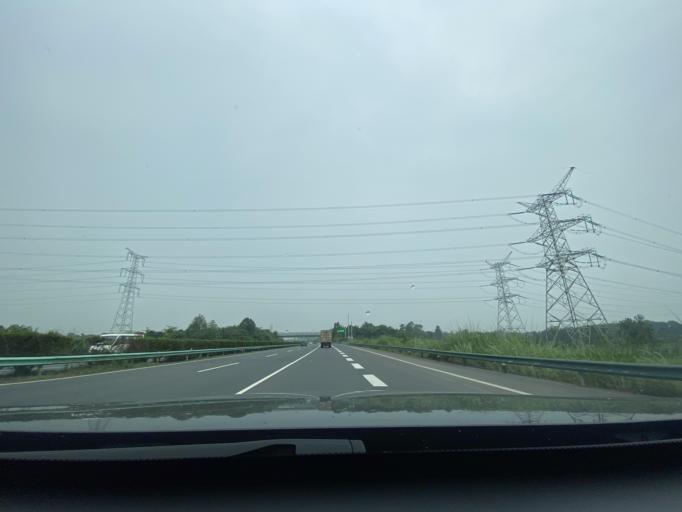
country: CN
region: Sichuan
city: Longquan
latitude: 30.3348
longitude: 104.1194
